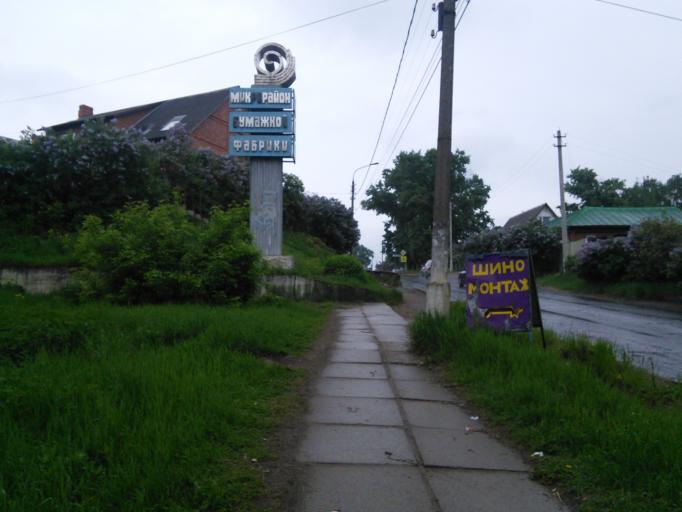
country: RU
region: Moskovskaya
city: Serpukhov
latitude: 54.9232
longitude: 37.3789
